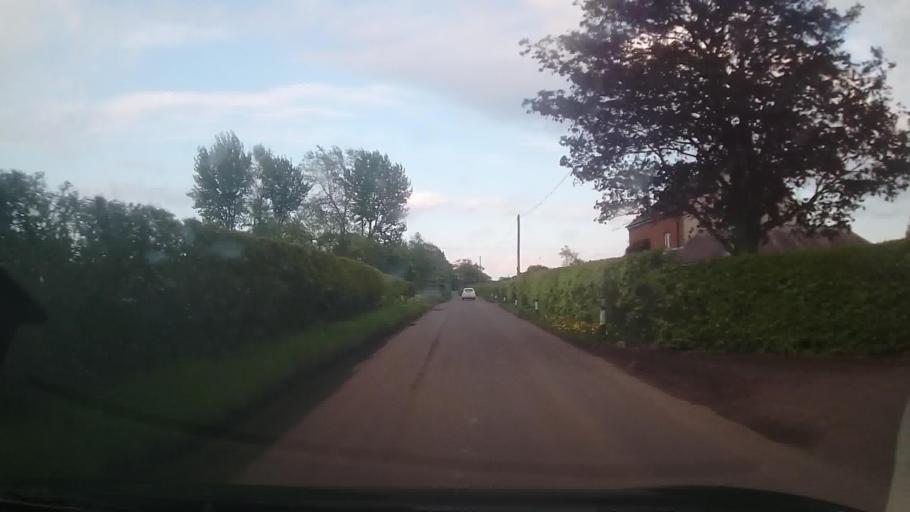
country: GB
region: England
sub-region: Shropshire
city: Ellesmere
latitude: 52.9372
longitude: -2.8845
